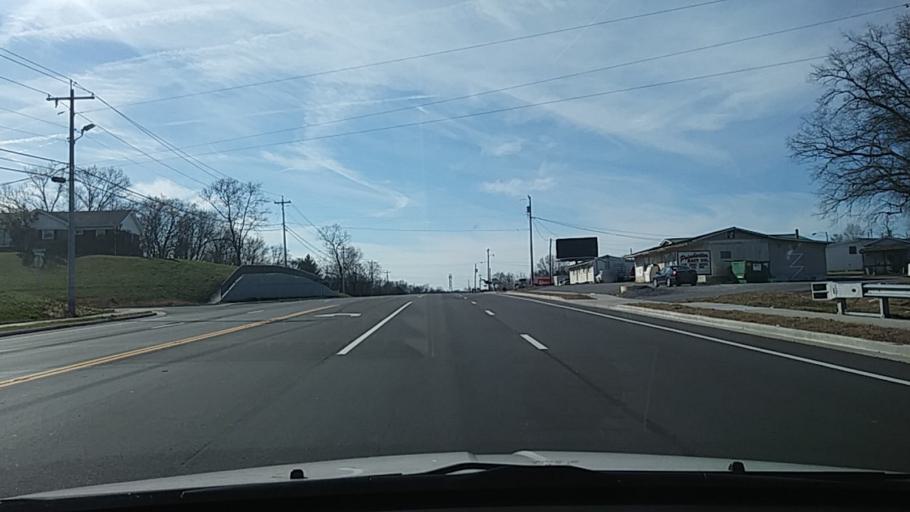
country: US
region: Tennessee
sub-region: Sumner County
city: Gallatin
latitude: 36.3549
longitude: -86.4389
